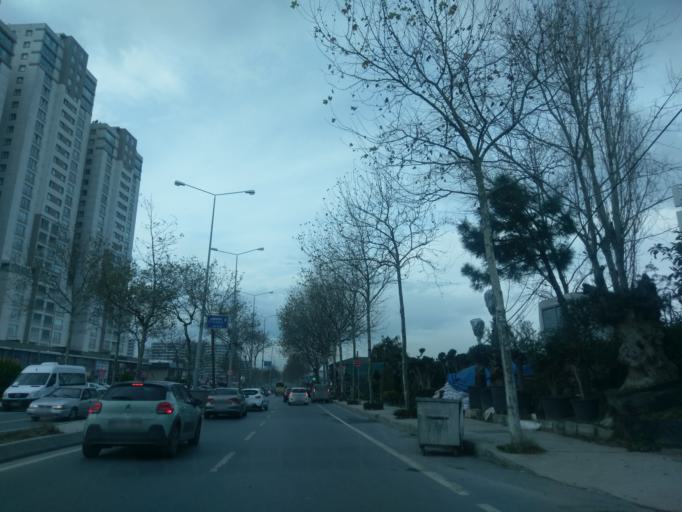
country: TR
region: Istanbul
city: Esenyurt
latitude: 41.0653
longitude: 28.6717
